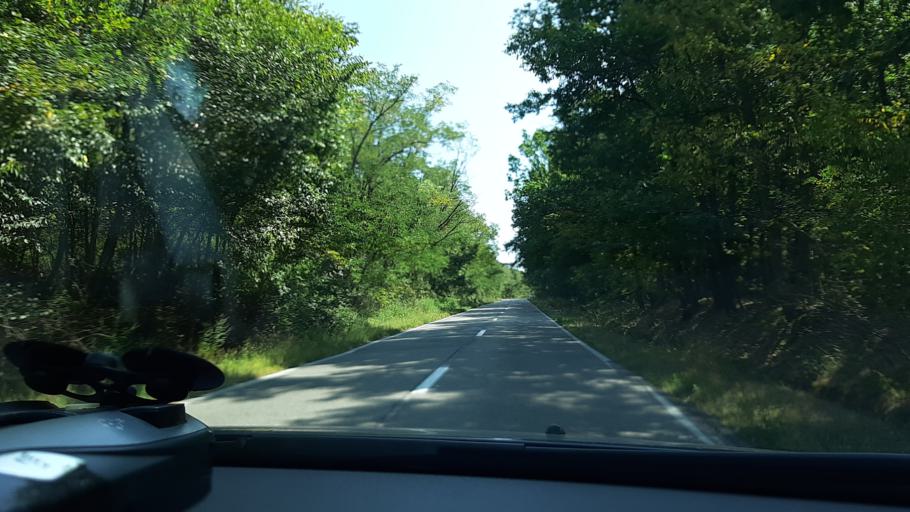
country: RO
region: Gorj
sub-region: Comuna Targu Carbunesti
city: Targu Carbunesti
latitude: 44.9492
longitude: 23.5592
